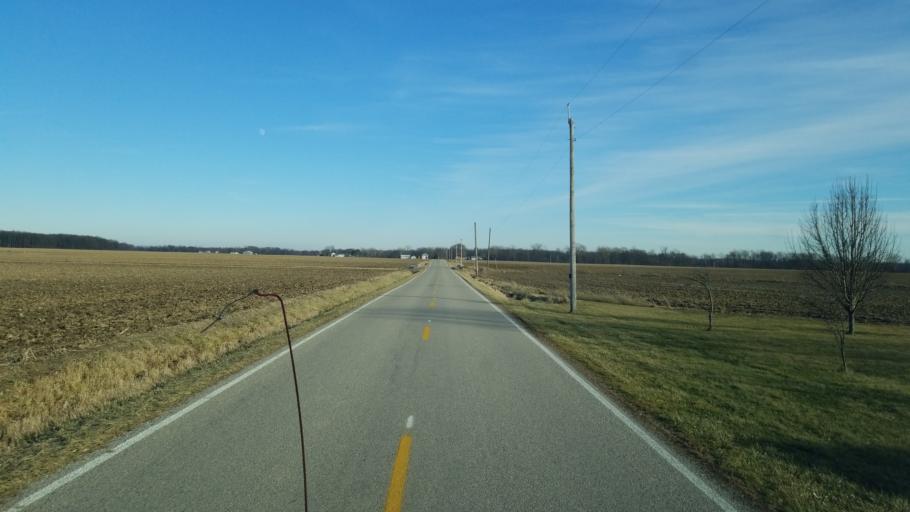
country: US
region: Ohio
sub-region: Huron County
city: Monroeville
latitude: 41.1793
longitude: -82.7759
